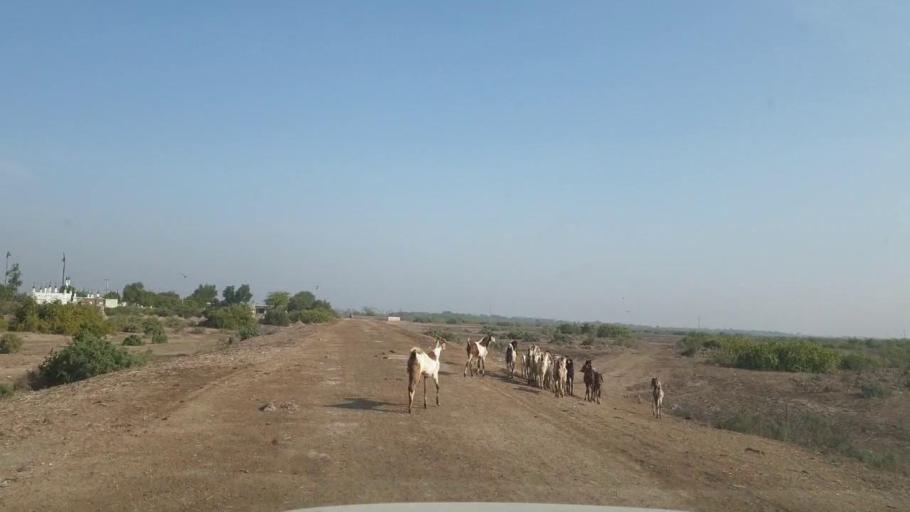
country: PK
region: Sindh
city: Mirpur Khas
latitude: 25.5039
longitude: 69.0475
